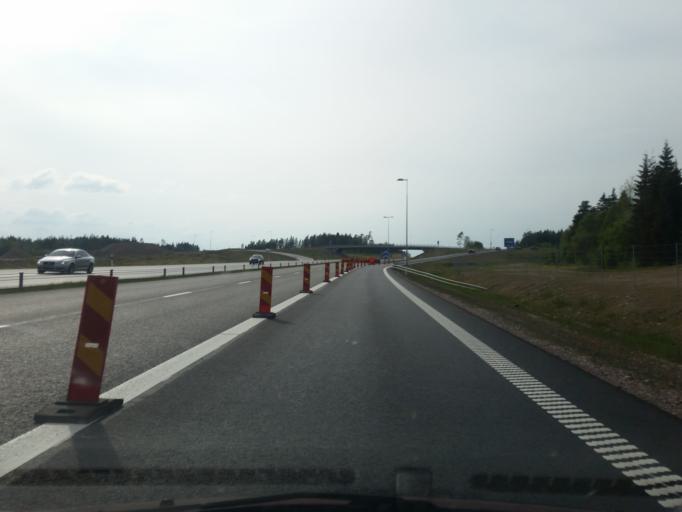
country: SE
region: Vaestra Goetaland
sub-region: Ulricehamns Kommun
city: Ulricehamn
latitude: 57.8034
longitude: 13.4780
